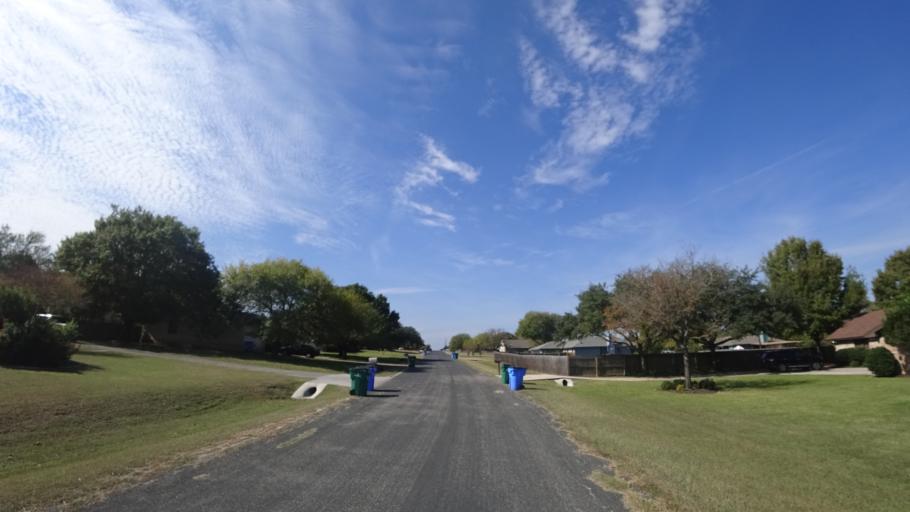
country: US
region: Texas
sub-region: Travis County
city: Pflugerville
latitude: 30.4114
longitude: -97.6268
